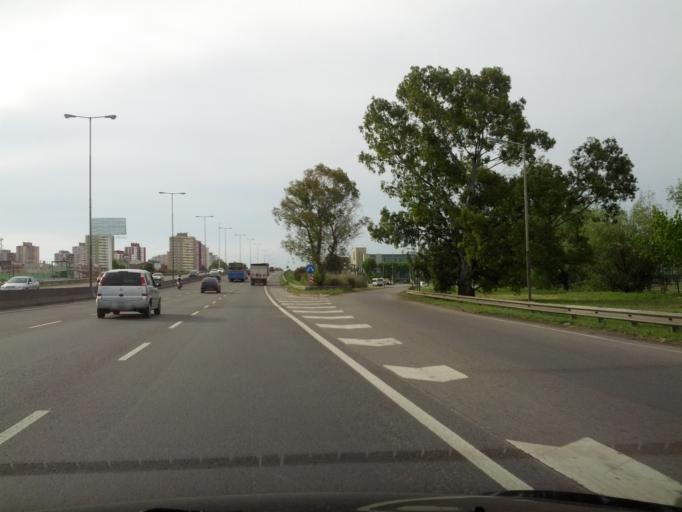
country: AR
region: Buenos Aires F.D.
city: Villa Lugano
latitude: -34.7003
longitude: -58.4676
